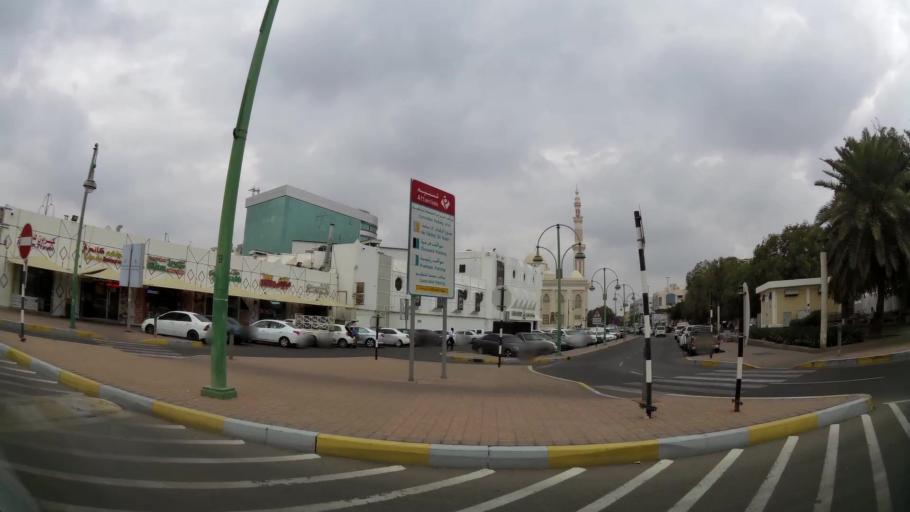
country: AE
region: Abu Dhabi
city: Al Ain
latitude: 24.2201
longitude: 55.7705
